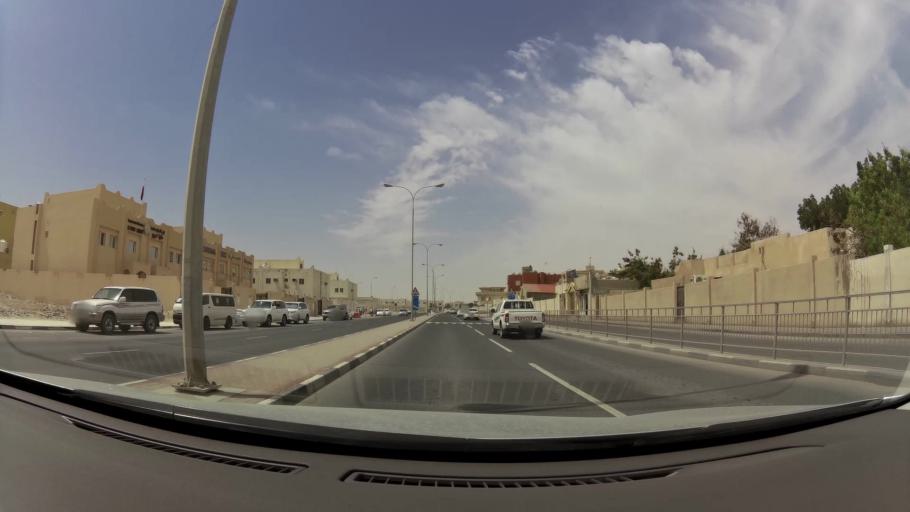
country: QA
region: Baladiyat ar Rayyan
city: Ar Rayyan
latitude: 25.2862
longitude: 51.4221
